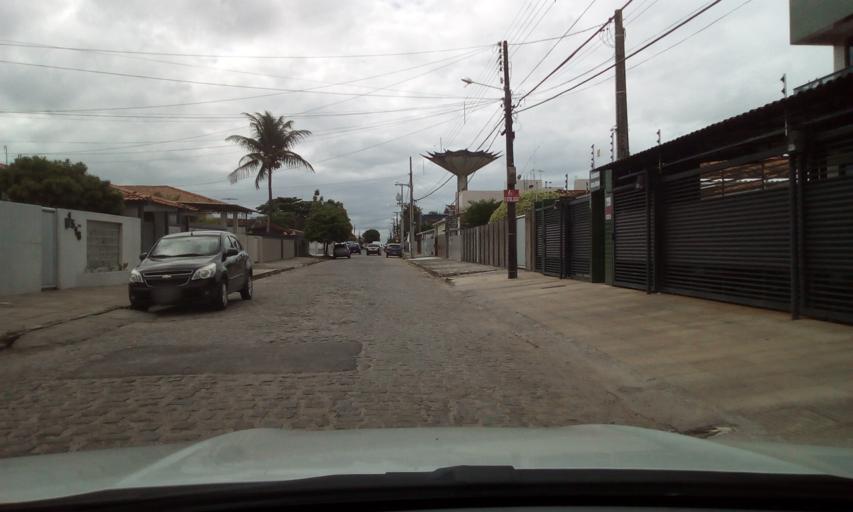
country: BR
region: Paraiba
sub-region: Joao Pessoa
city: Joao Pessoa
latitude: -7.1569
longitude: -34.8719
